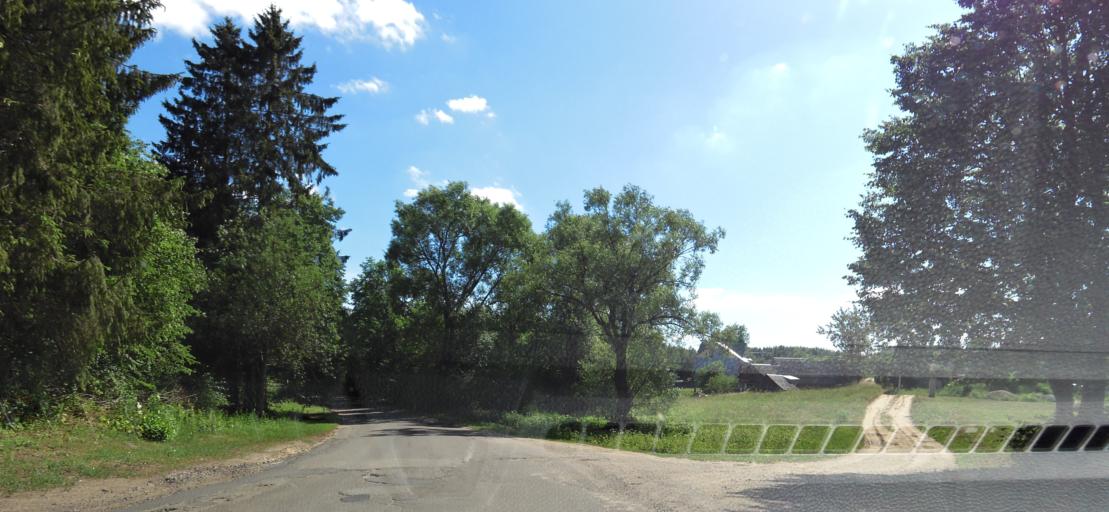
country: LT
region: Vilnius County
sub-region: Vilnius
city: Fabijoniskes
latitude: 54.8143
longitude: 25.3218
